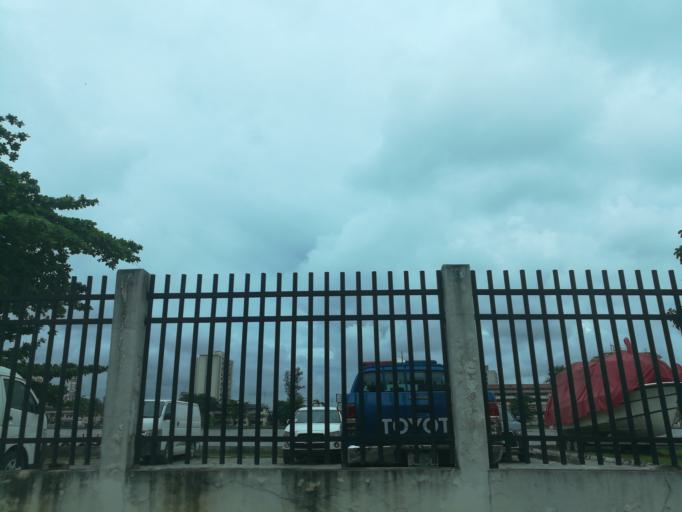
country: NG
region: Lagos
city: Lagos
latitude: 6.4410
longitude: 3.4074
